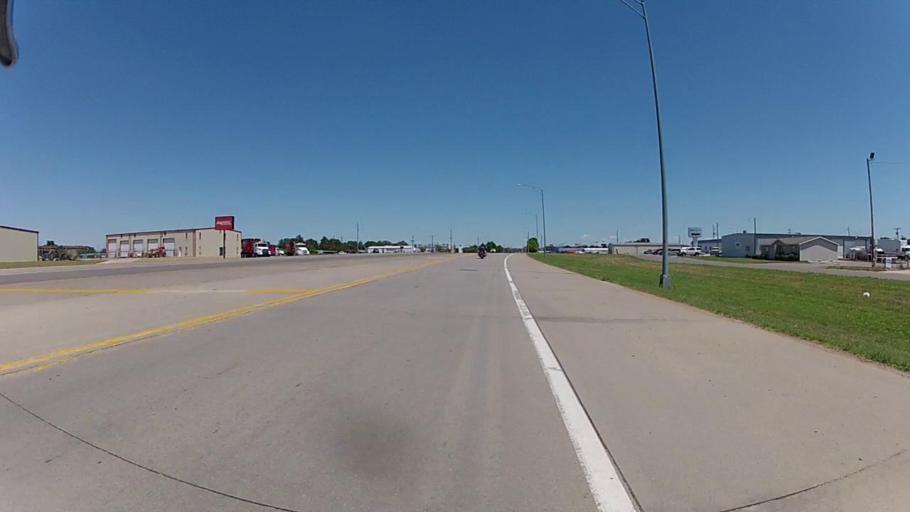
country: US
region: Kansas
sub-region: Ford County
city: Dodge City
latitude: 37.7322
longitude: -100.0193
